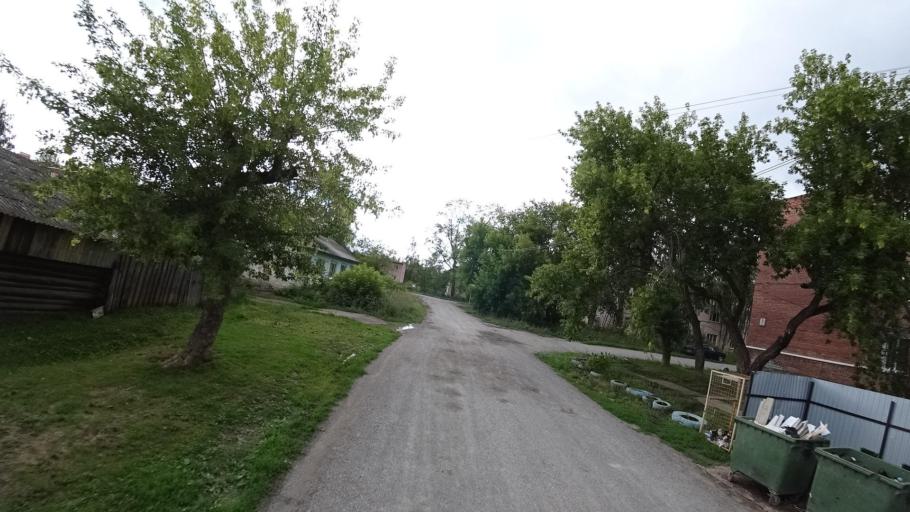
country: RU
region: Sverdlovsk
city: Kamyshlov
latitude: 56.8530
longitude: 62.7297
